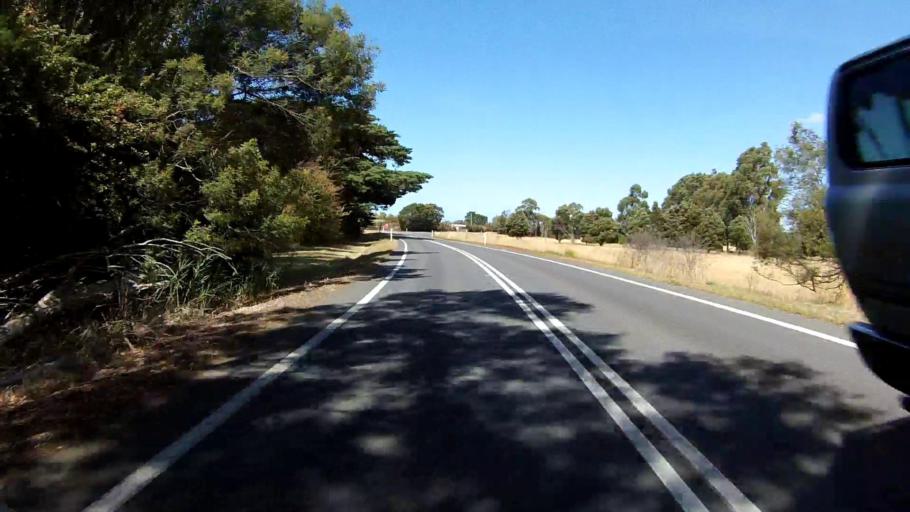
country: AU
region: Tasmania
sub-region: Break O'Day
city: St Helens
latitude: -42.0687
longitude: 148.0643
